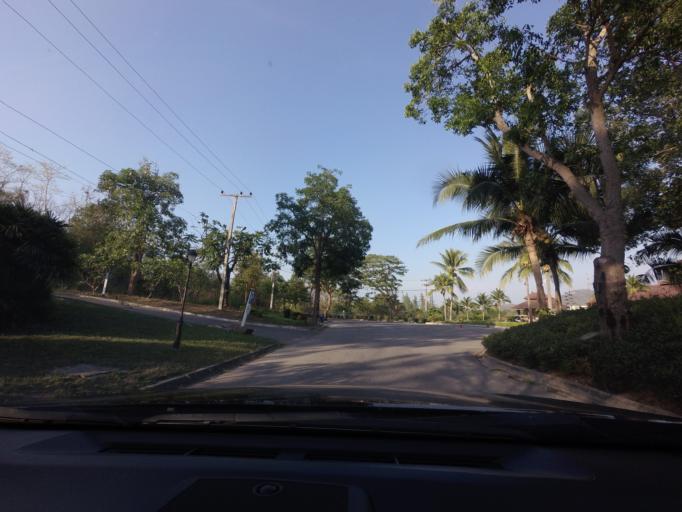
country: TH
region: Phetchaburi
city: Cha-am
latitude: 12.7097
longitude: 99.8652
